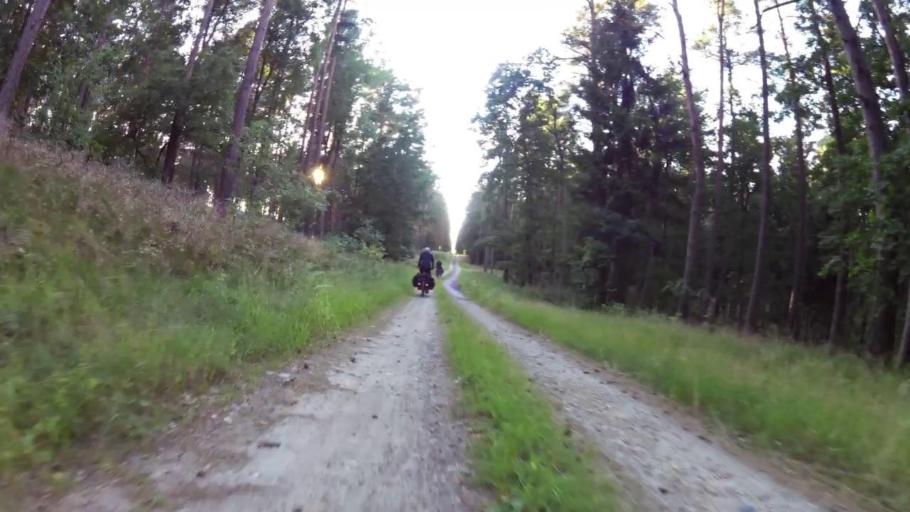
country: PL
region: West Pomeranian Voivodeship
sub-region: Powiat lobeski
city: Lobez
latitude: 53.7409
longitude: 15.6540
